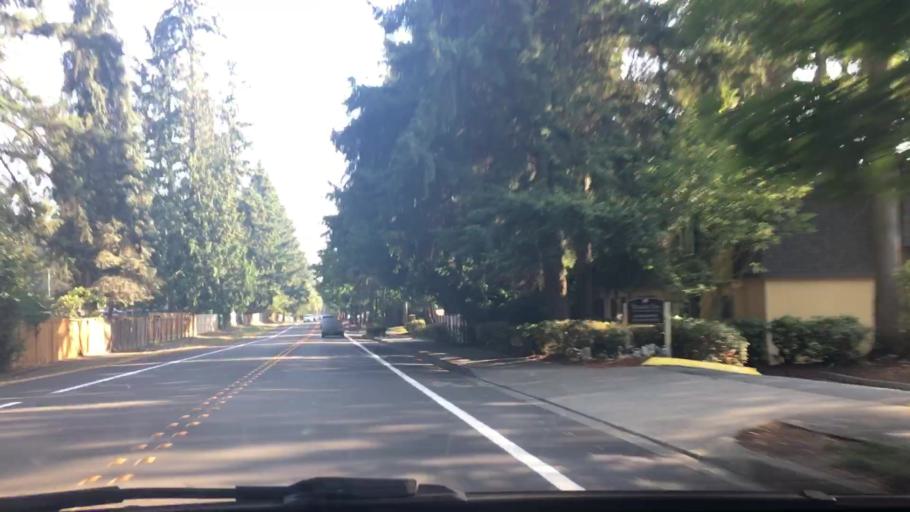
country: US
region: Washington
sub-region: King County
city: Sammamish
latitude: 47.6233
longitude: -122.1217
